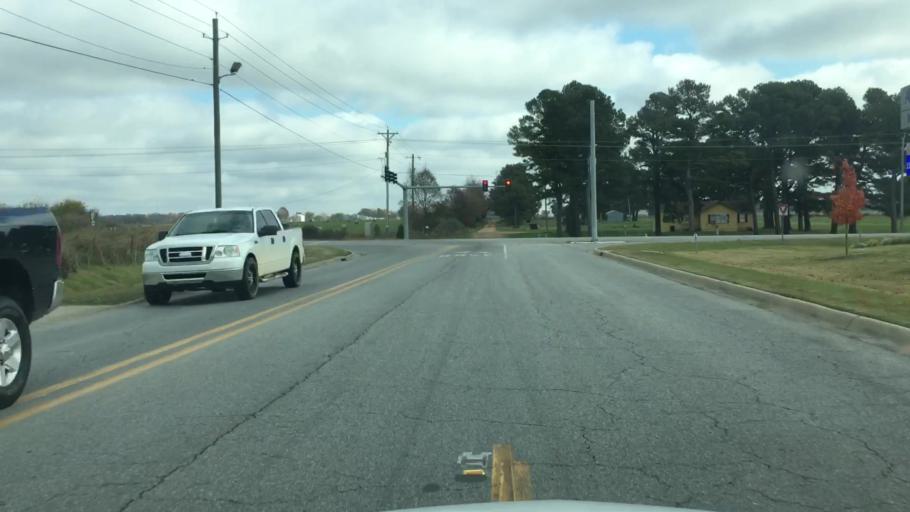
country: US
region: Arkansas
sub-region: Benton County
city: Siloam Springs
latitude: 36.1952
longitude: -94.4970
